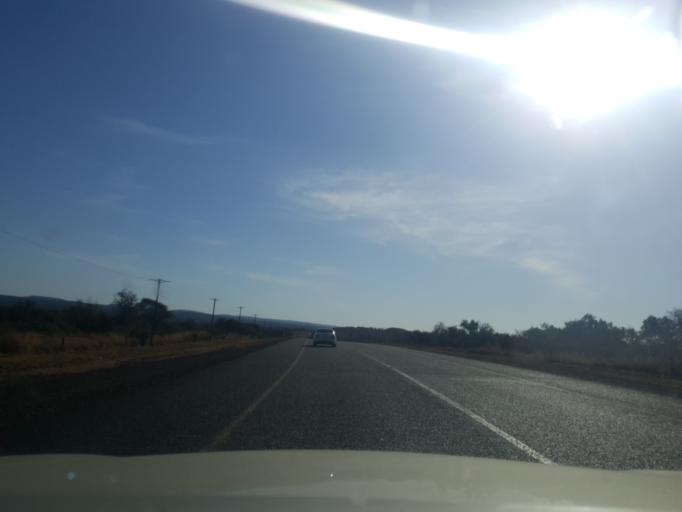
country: ZA
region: North-West
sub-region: Ngaka Modiri Molema District Municipality
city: Zeerust
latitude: -25.5390
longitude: 26.0394
